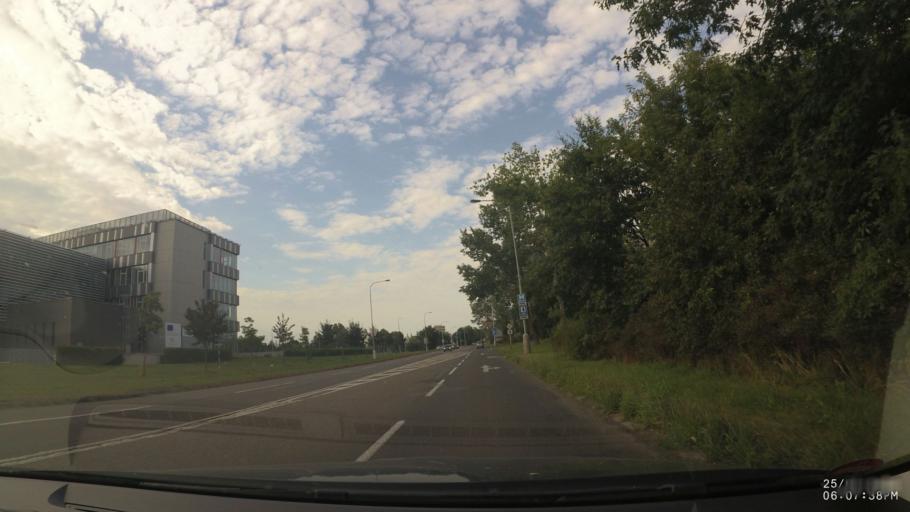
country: CZ
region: Kralovehradecky
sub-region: Okres Hradec Kralove
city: Hradec Kralove
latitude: 50.1971
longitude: 15.8316
